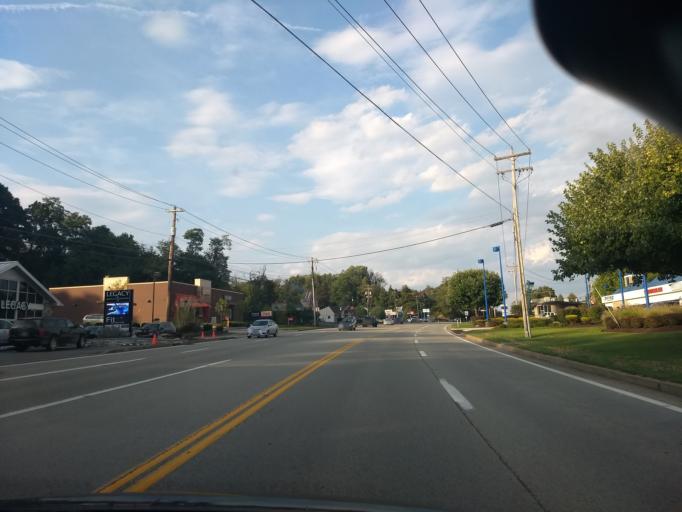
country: US
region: Pennsylvania
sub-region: Washington County
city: Thompsonville
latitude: 40.2831
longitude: -80.1216
